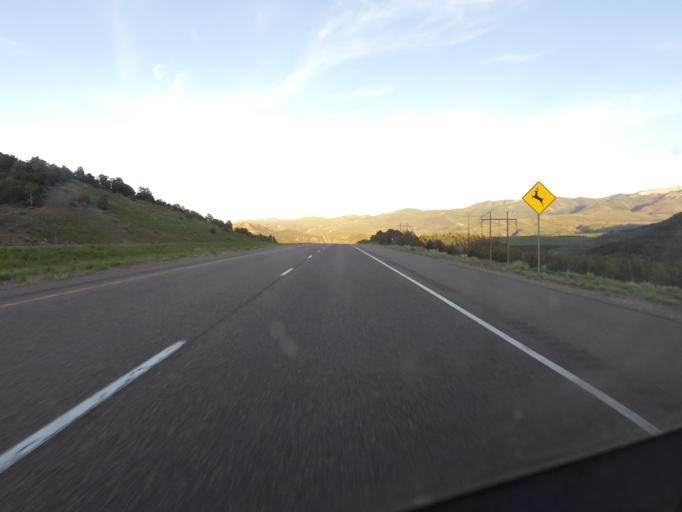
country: US
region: Utah
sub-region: Beaver County
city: Beaver
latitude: 38.5788
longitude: -112.4789
